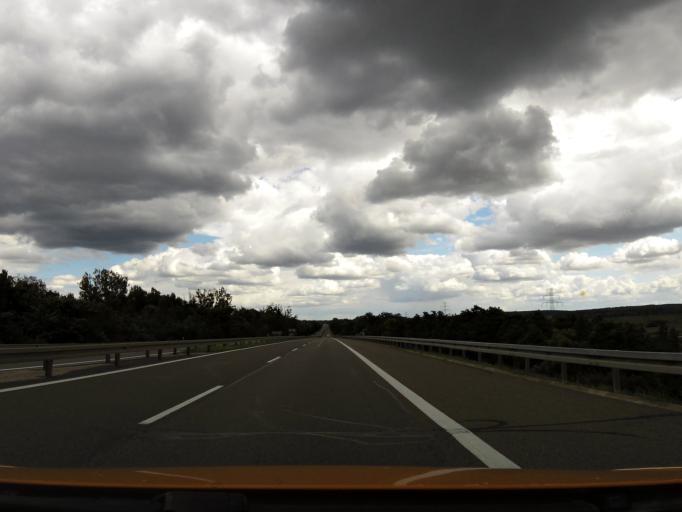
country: PL
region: West Pomeranian Voivodeship
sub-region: Powiat policki
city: Przeclaw
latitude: 53.3390
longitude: 14.5002
